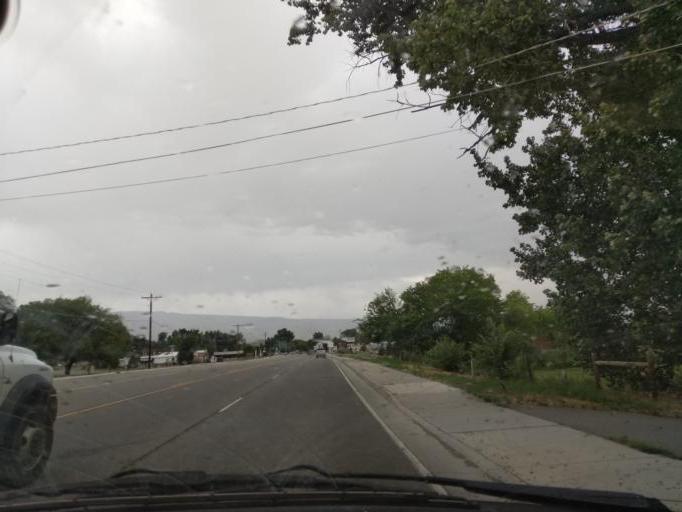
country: US
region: Colorado
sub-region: Delta County
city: Delta
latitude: 38.7553
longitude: -108.0692
